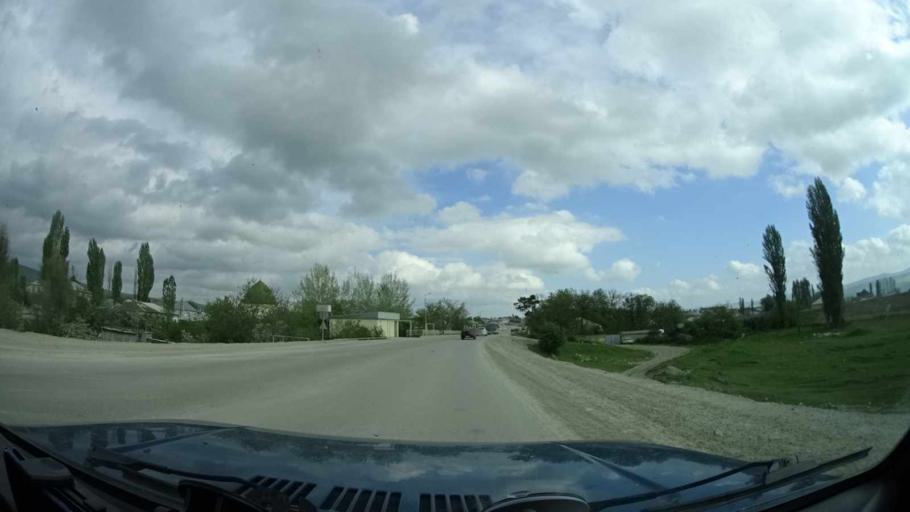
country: AZ
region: Samaxi
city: Shamakhi
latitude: 40.5948
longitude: 48.7017
